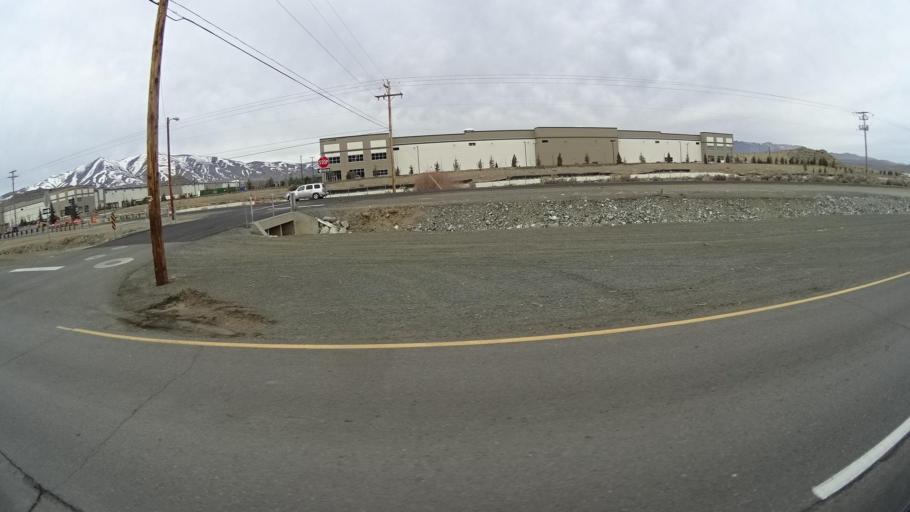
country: US
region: Nevada
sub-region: Washoe County
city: Lemmon Valley
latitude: 39.6325
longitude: -119.8449
